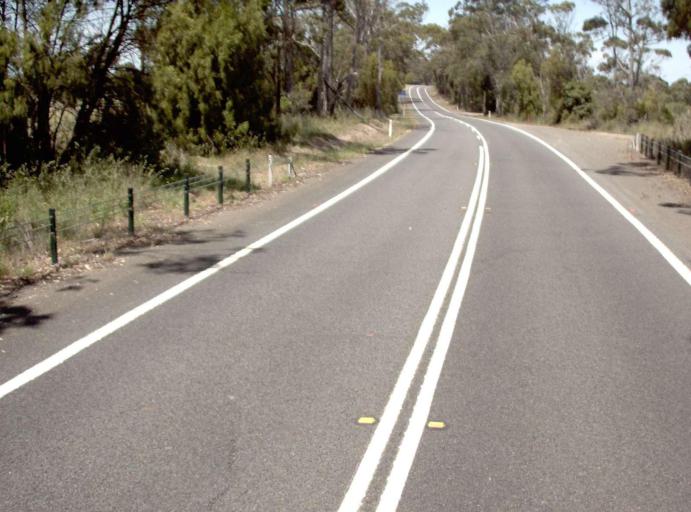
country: AU
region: Victoria
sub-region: East Gippsland
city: Lakes Entrance
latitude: -37.8391
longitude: 148.0339
